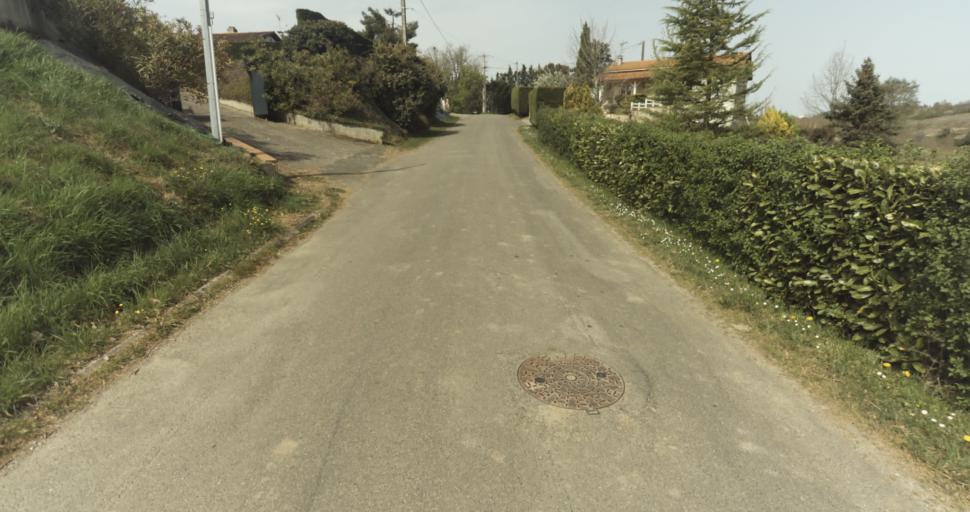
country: FR
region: Midi-Pyrenees
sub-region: Departement du Tarn-et-Garonne
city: Moissac
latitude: 44.1038
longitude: 1.0671
